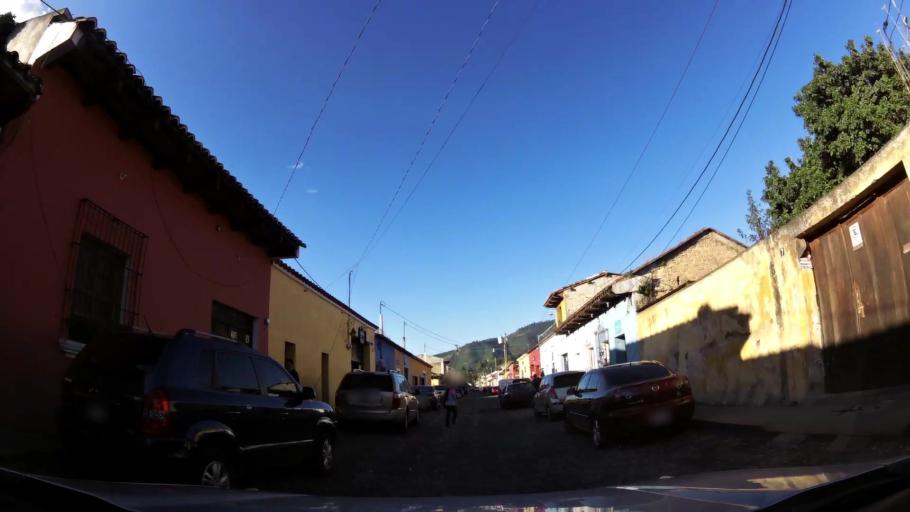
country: GT
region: Sacatepequez
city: Antigua Guatemala
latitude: 14.5588
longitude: -90.7363
